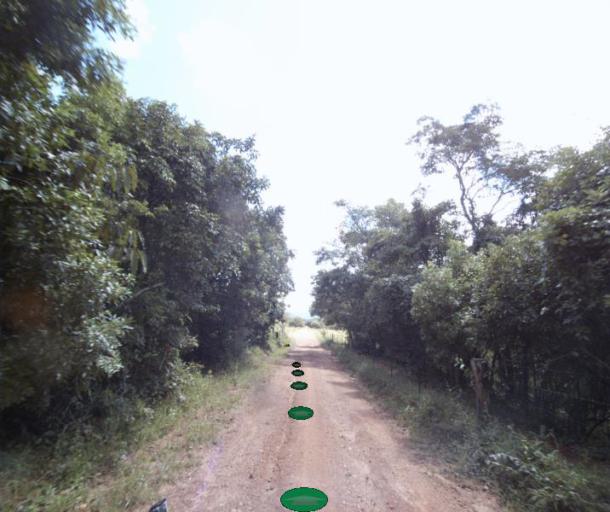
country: BR
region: Goias
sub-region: Pirenopolis
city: Pirenopolis
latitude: -15.7844
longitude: -48.9288
